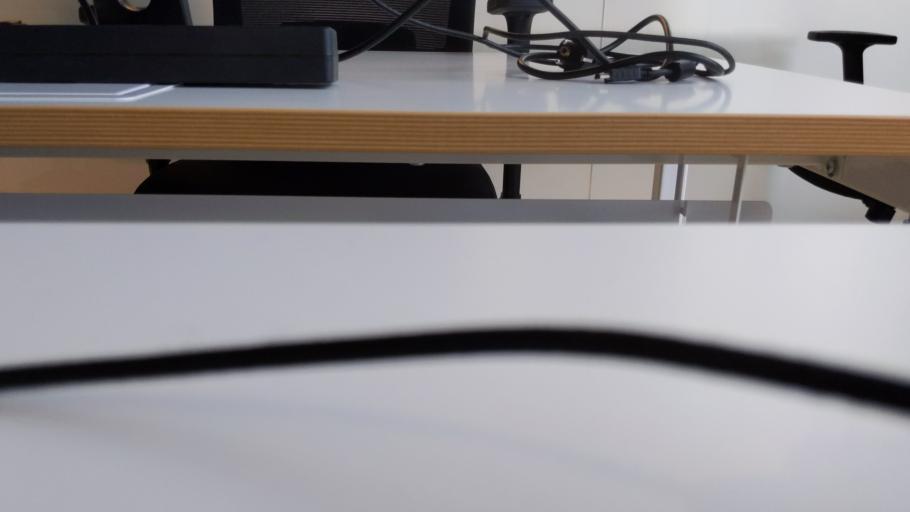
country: RU
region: Moskovskaya
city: Shevlyakovo
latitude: 56.4053
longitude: 36.9050
